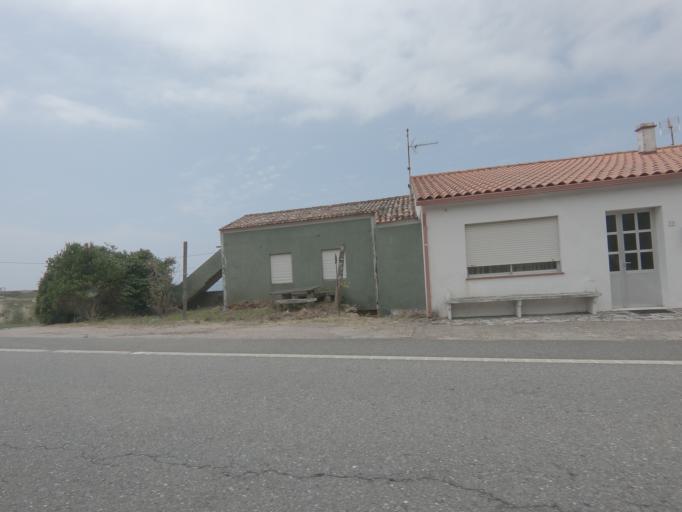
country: ES
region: Galicia
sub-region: Provincia de Pontevedra
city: O Rosal
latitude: 41.9521
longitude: -8.8824
